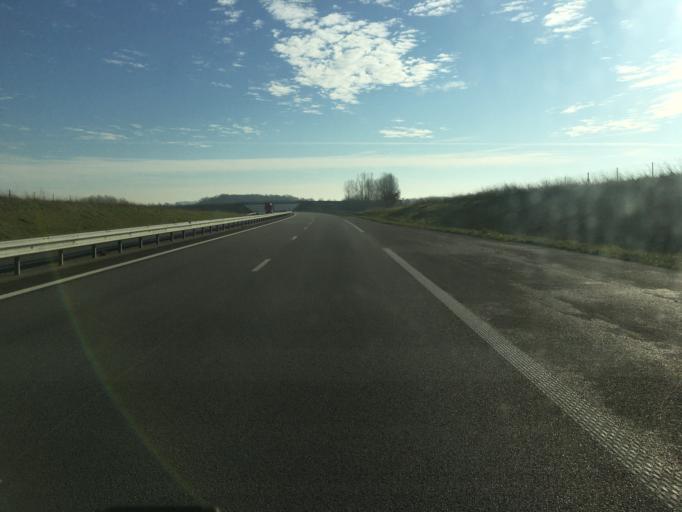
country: FR
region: Haute-Normandie
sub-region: Departement de la Seine-Maritime
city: Limesy
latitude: 49.6511
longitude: 0.9544
